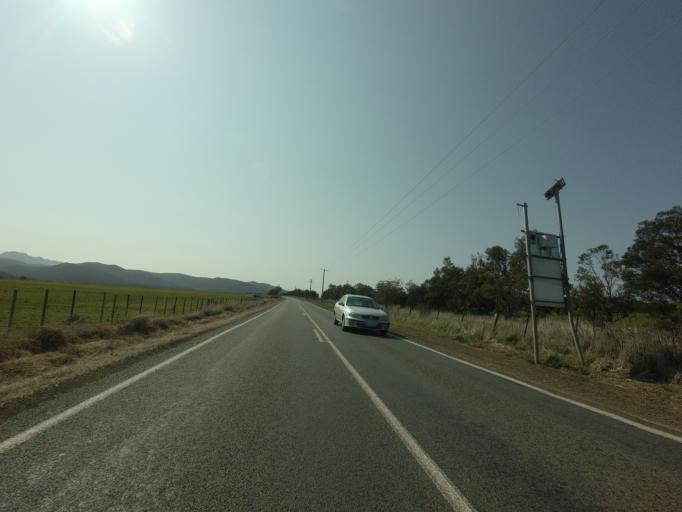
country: AU
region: Tasmania
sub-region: Northern Midlands
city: Evandale
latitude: -41.7960
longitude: 147.7072
